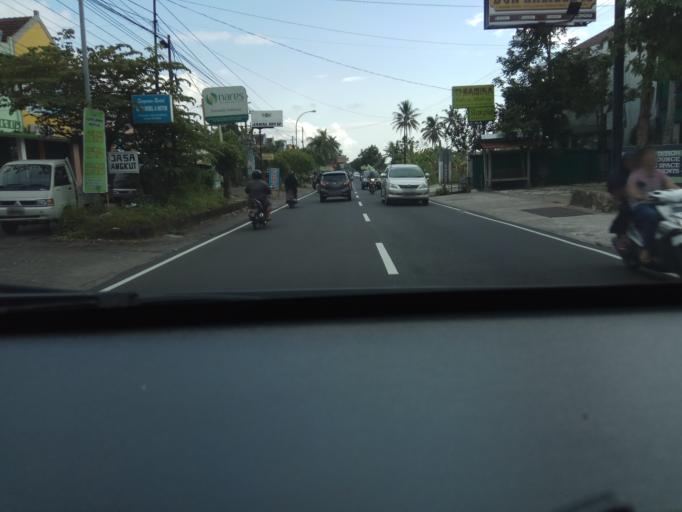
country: ID
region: Daerah Istimewa Yogyakarta
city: Melati
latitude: -7.7076
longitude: 110.4108
